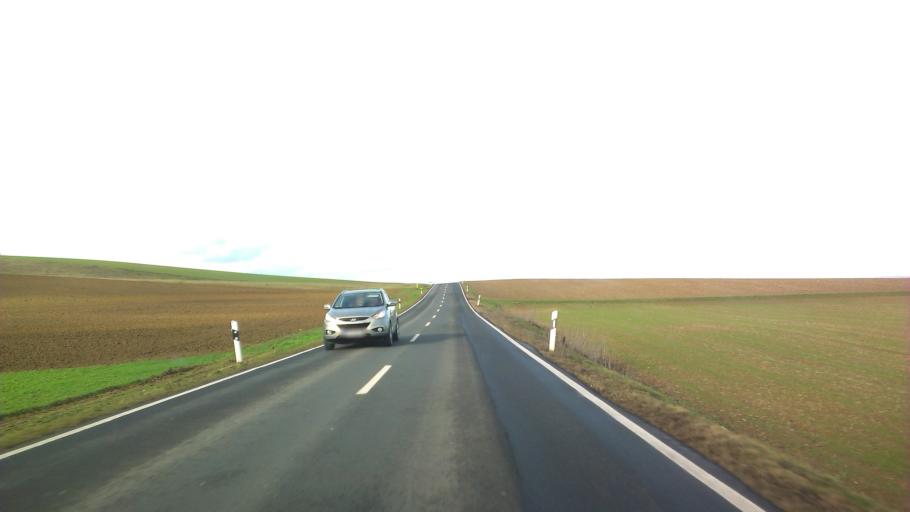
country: DE
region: Rheinland-Pfalz
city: Wendelsheim
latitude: 49.7757
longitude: 7.9870
